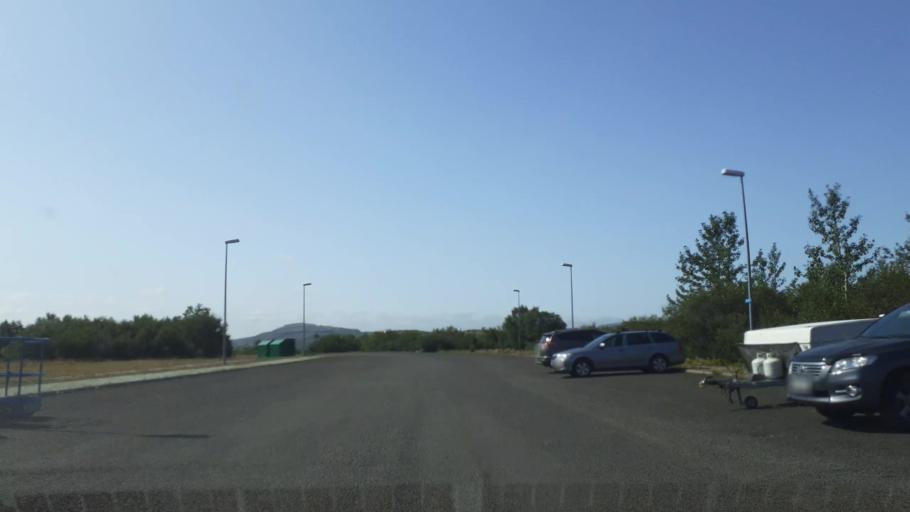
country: IS
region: West
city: Borgarnes
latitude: 64.7667
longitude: -21.5534
